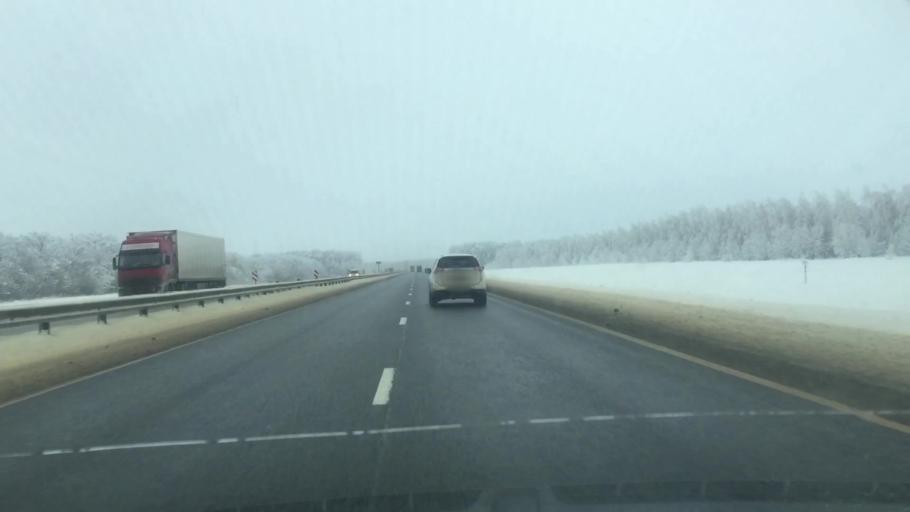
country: RU
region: Lipetsk
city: Zadonsk
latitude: 52.4983
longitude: 38.7555
